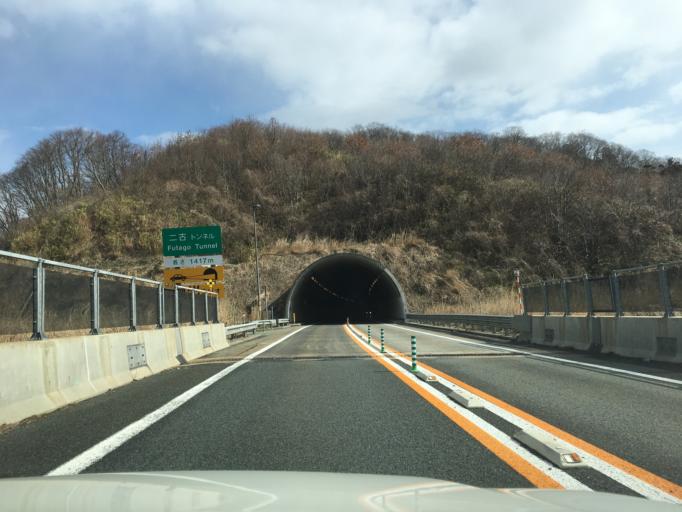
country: JP
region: Akita
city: Akita Shi
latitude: 39.5303
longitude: 140.0639
